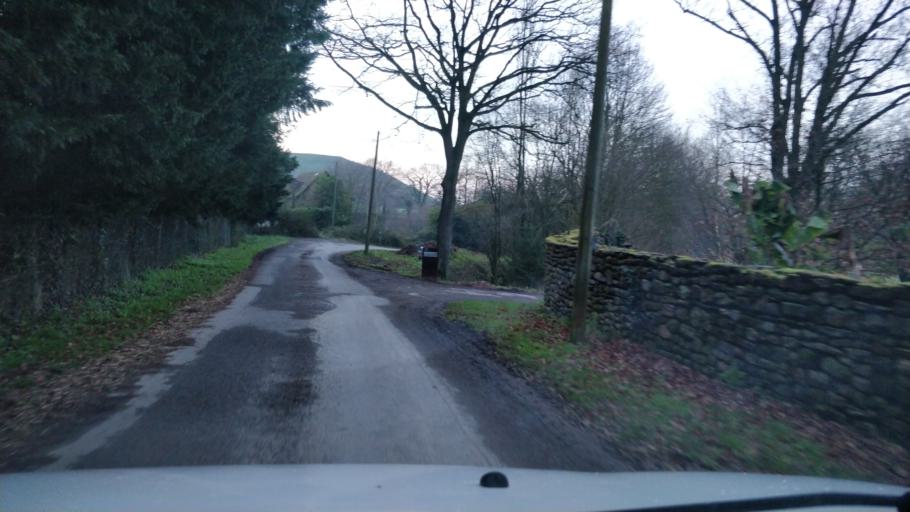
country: FR
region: Brittany
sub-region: Departement d'Ille-et-Vilaine
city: Louvigne-de-Bais
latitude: 48.0418
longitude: -1.3382
